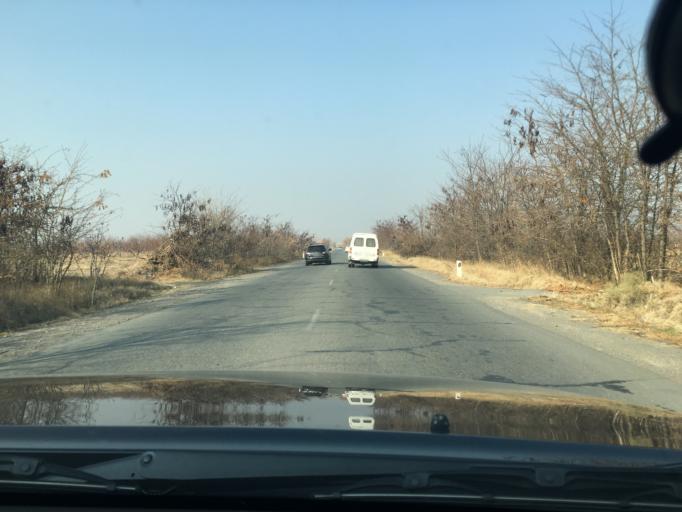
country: AM
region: Armavir
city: Myasnikyan
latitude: 40.1788
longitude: 43.9319
